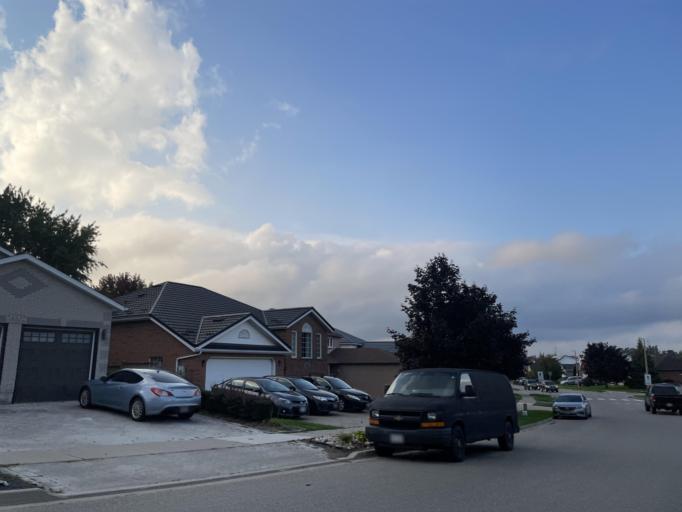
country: CA
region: Ontario
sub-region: Wellington County
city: Guelph
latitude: 43.5252
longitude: -80.2737
